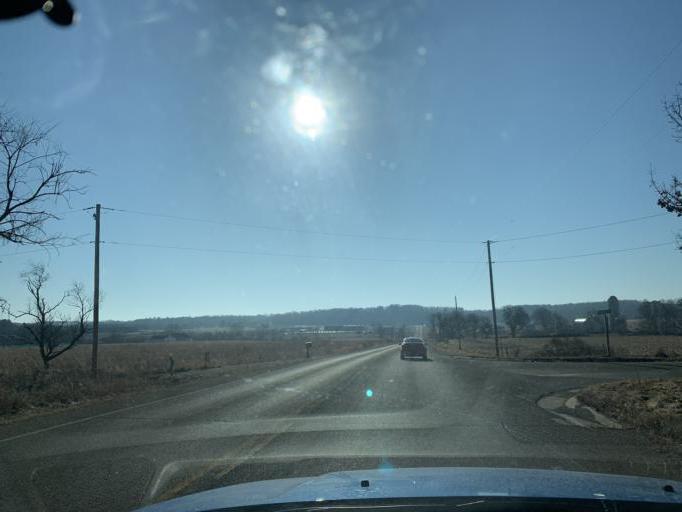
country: US
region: Wisconsin
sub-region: Dane County
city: Belleville
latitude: 42.8716
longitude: -89.5601
